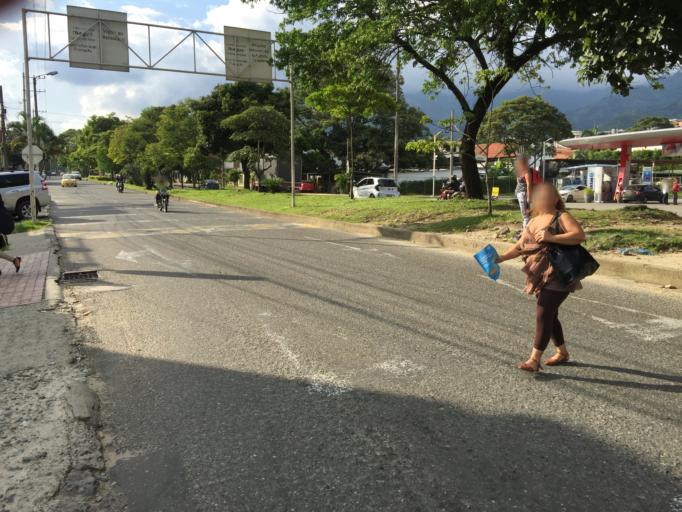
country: CO
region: Tolima
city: Ibague
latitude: 4.4465
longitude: -75.1908
